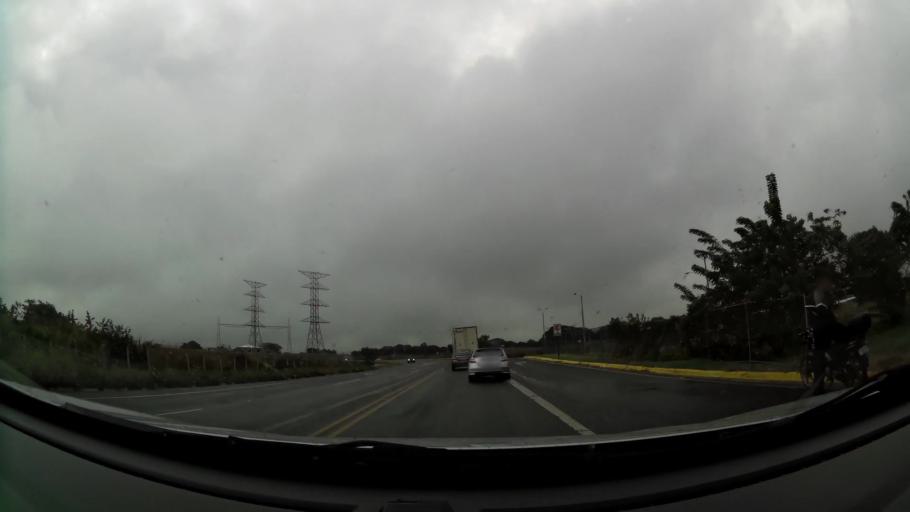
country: CR
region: Alajuela
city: Carrillos
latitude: 9.9903
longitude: -84.2690
